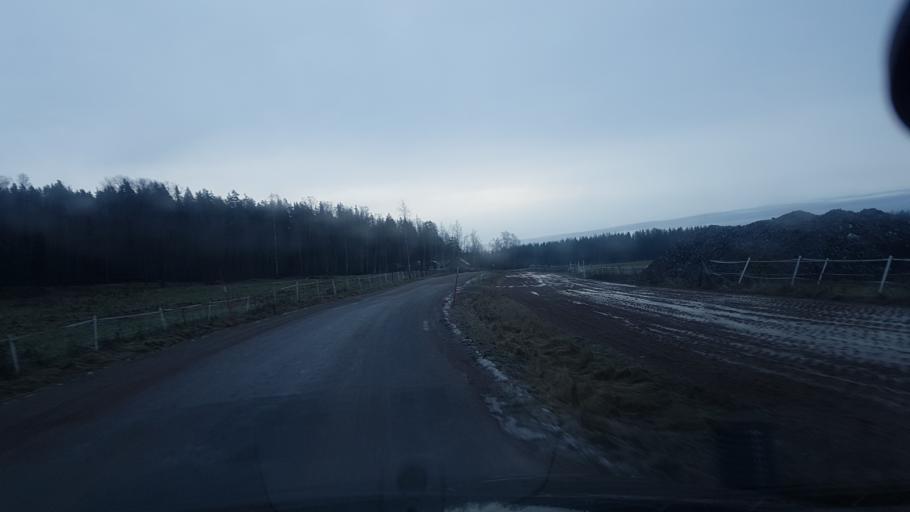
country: SE
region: Dalarna
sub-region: Borlange Kommun
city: Ornas
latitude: 60.4432
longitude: 15.6438
